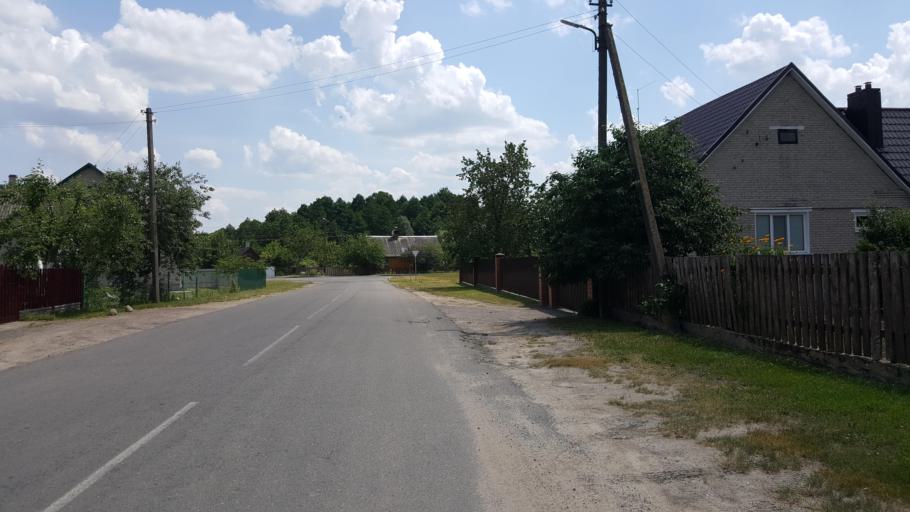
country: BY
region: Brest
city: Kamyanyets
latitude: 52.4016
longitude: 23.7921
